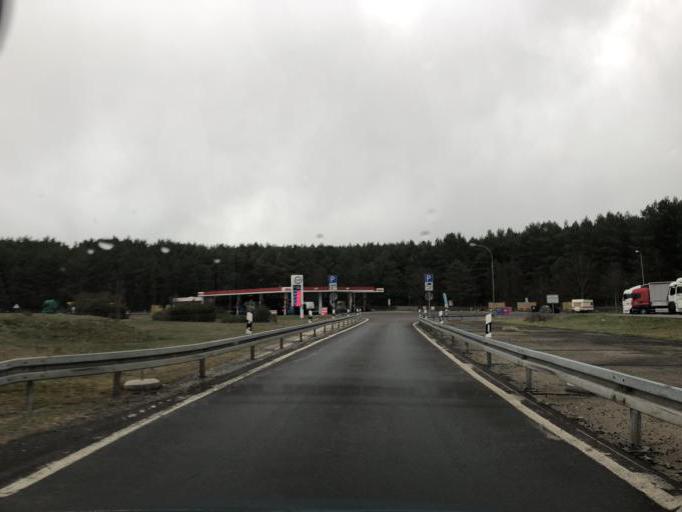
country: DE
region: Brandenburg
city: Kremmen
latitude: 52.6851
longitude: 13.0088
